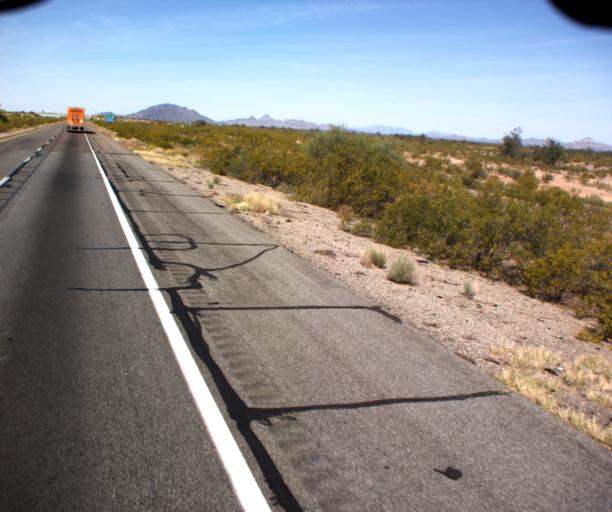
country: US
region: Arizona
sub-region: Maricopa County
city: Buckeye
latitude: 33.4953
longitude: -112.9270
